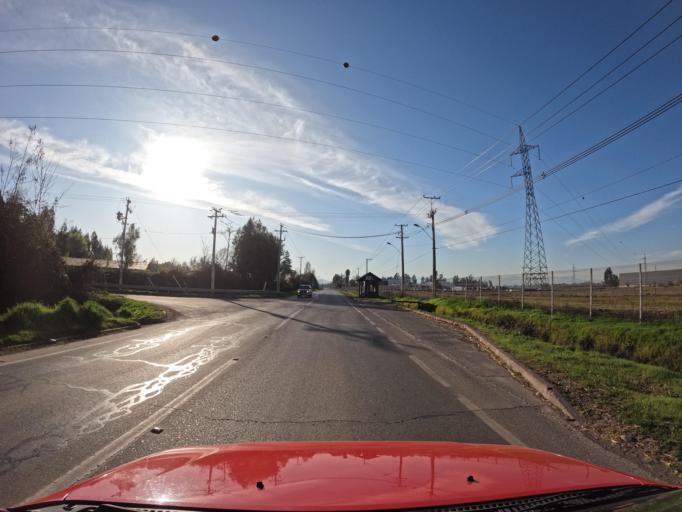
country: CL
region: Maule
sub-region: Provincia de Curico
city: Teno
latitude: -34.8635
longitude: -71.0932
